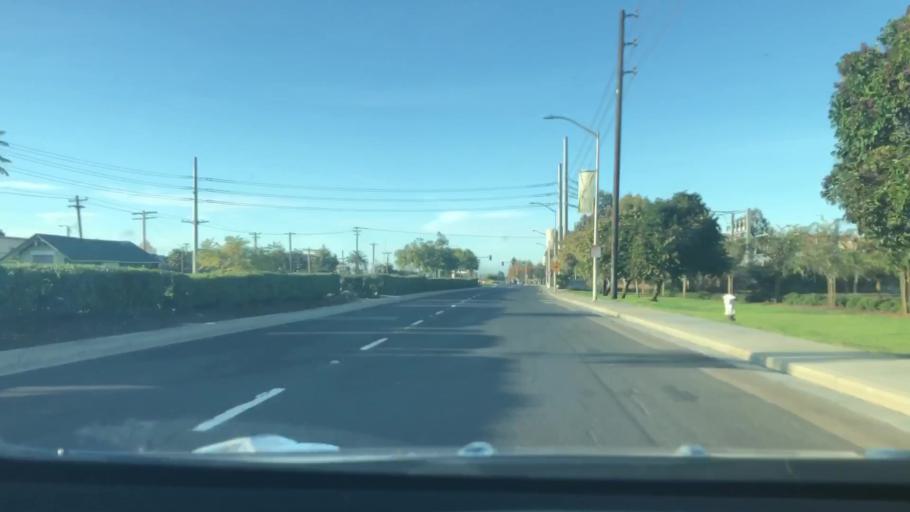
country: US
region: California
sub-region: Santa Clara County
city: Santa Clara
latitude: 37.3931
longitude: -121.9573
